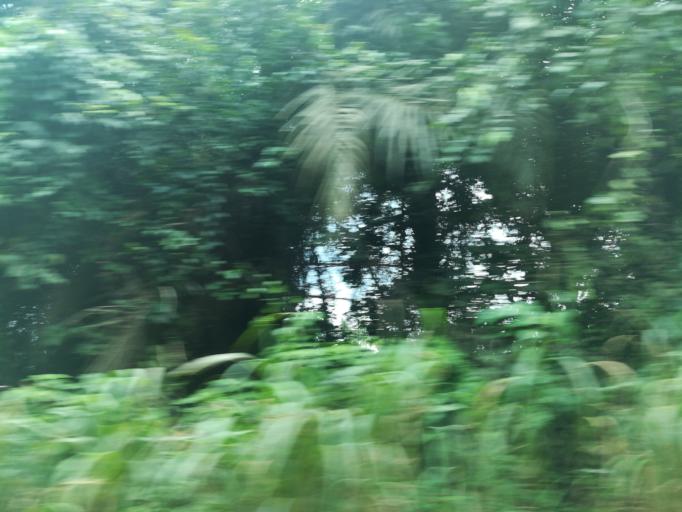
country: NG
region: Lagos
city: Ejirin
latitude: 6.6484
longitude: 3.7418
